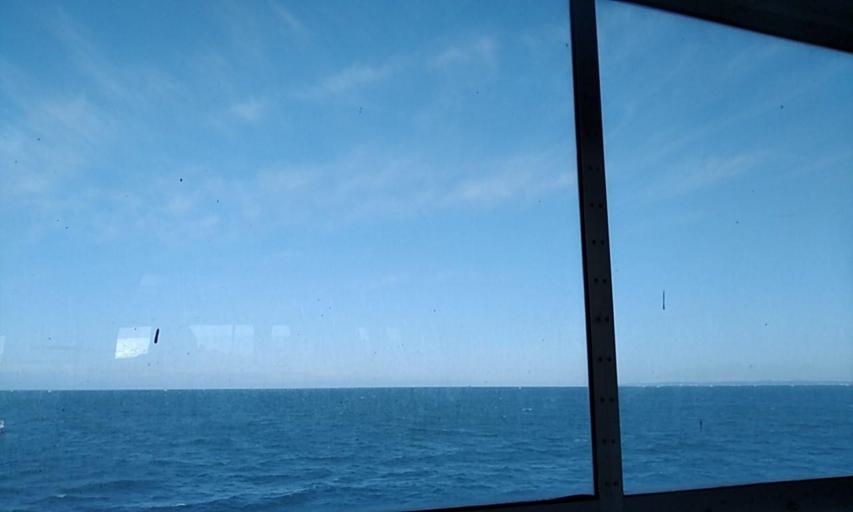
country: JP
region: Mie
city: Toba
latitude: 34.5430
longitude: 136.9594
